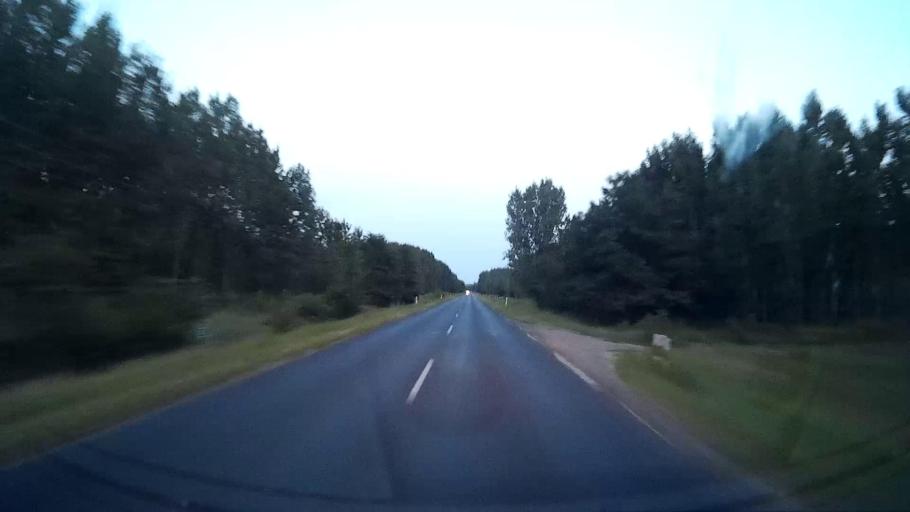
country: HU
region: Pest
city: Cegledbercel
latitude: 47.2010
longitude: 19.7034
